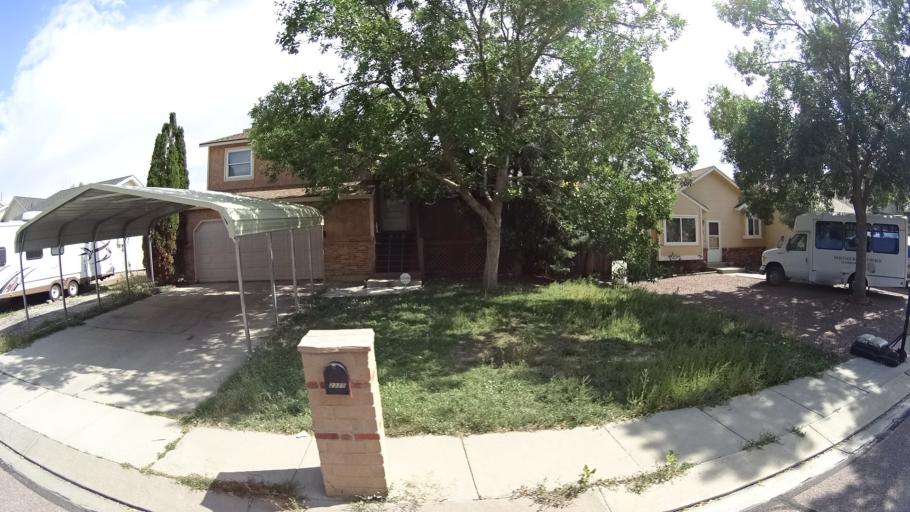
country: US
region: Colorado
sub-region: El Paso County
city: Cimarron Hills
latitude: 38.8658
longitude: -104.7241
